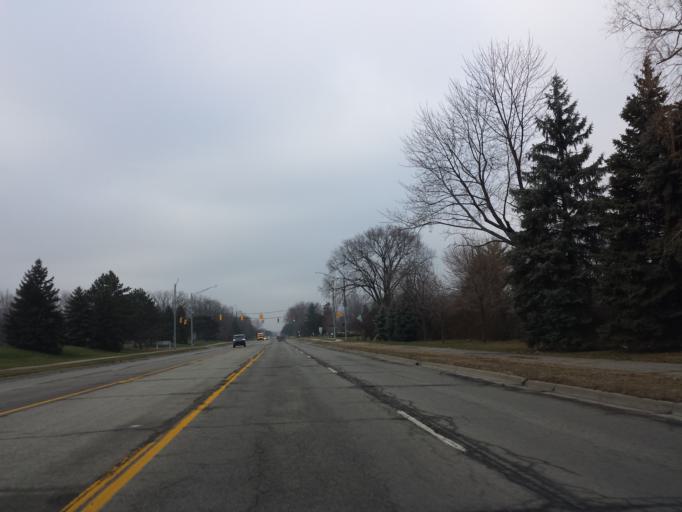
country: US
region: Michigan
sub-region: Oakland County
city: Bingham Farms
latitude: 42.5018
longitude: -83.2504
